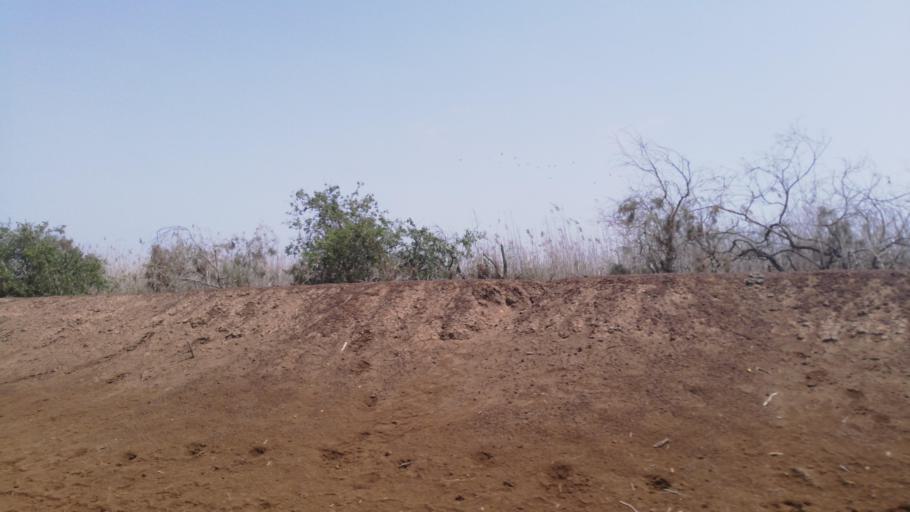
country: SN
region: Saint-Louis
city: Saint-Louis
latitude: 16.4001
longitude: -16.2892
